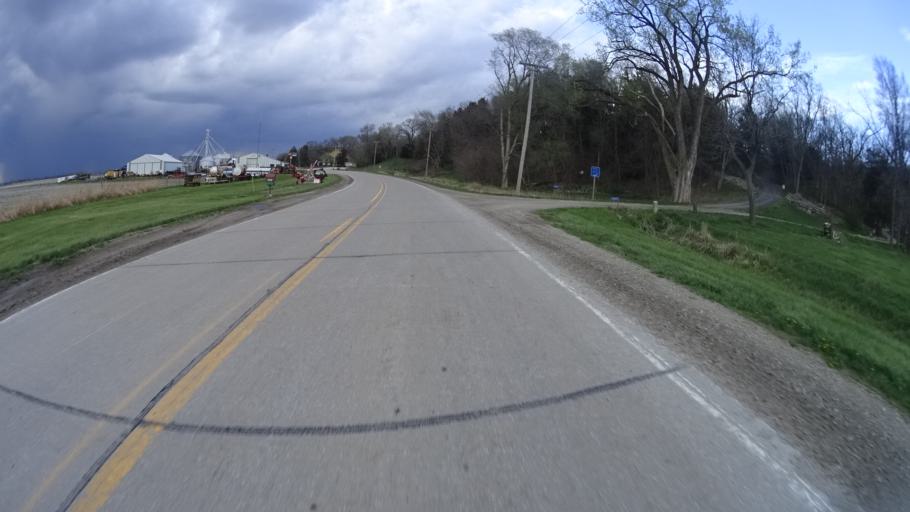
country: US
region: Iowa
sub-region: Mills County
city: Glenwood
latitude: 41.0591
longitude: -95.8036
